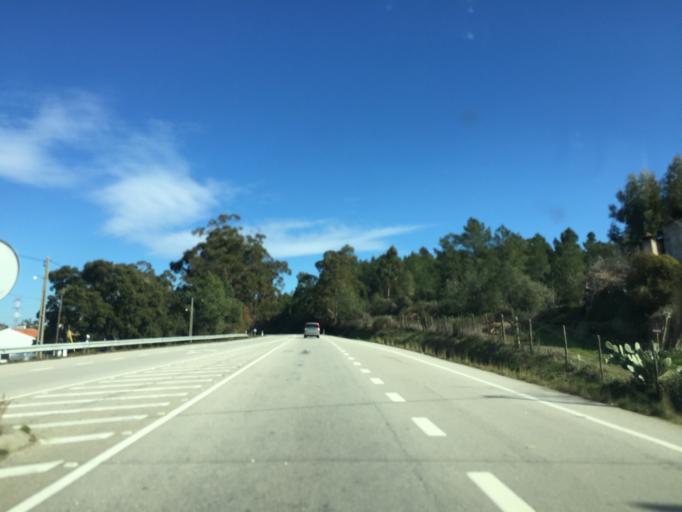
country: PT
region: Castelo Branco
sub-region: Castelo Branco
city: Castelo Branco
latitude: 39.7686
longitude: -7.5904
